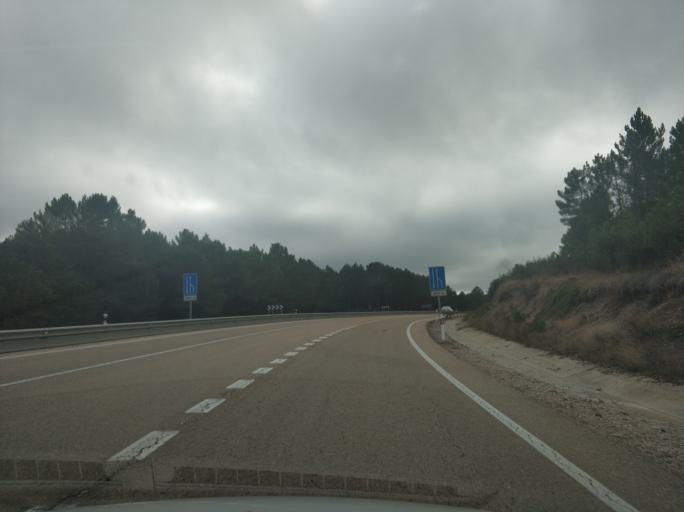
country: ES
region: Castille and Leon
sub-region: Provincia de Soria
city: Muriel Viejo
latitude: 41.8277
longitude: -2.9462
